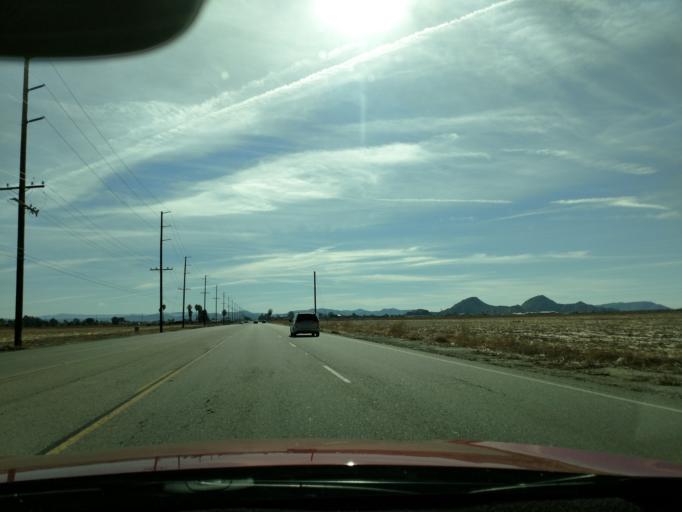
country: US
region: California
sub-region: Riverside County
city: San Jacinto
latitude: 33.7960
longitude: -117.0068
